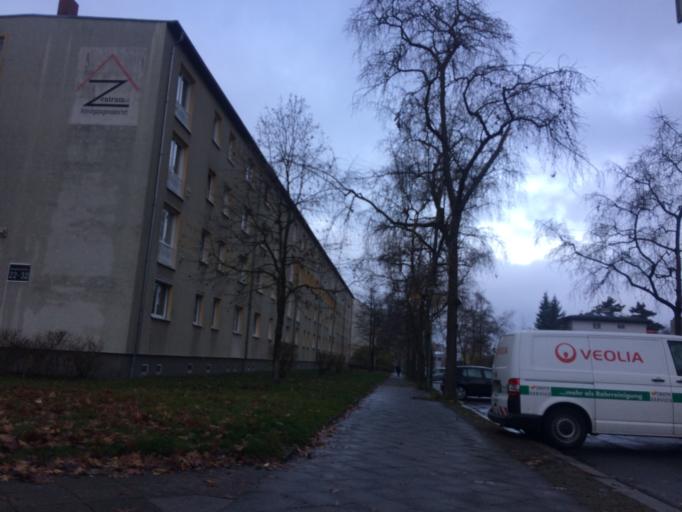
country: DE
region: Berlin
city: Fennpfuhl
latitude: 52.5329
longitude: 13.4606
